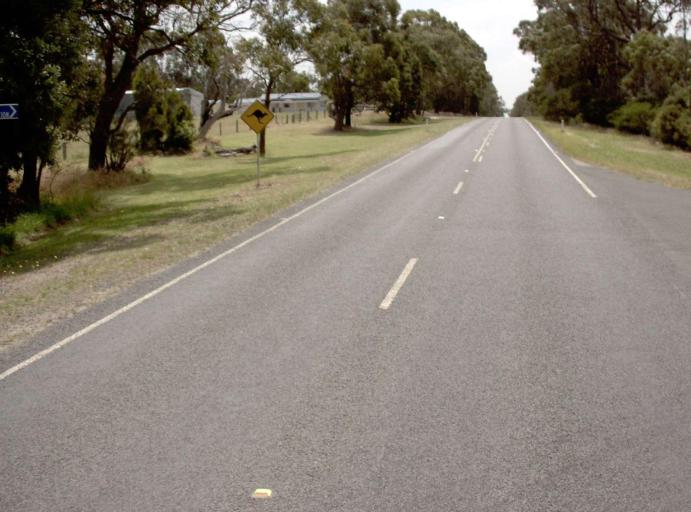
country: AU
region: Victoria
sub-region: Latrobe
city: Traralgon
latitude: -38.5415
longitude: 146.7024
